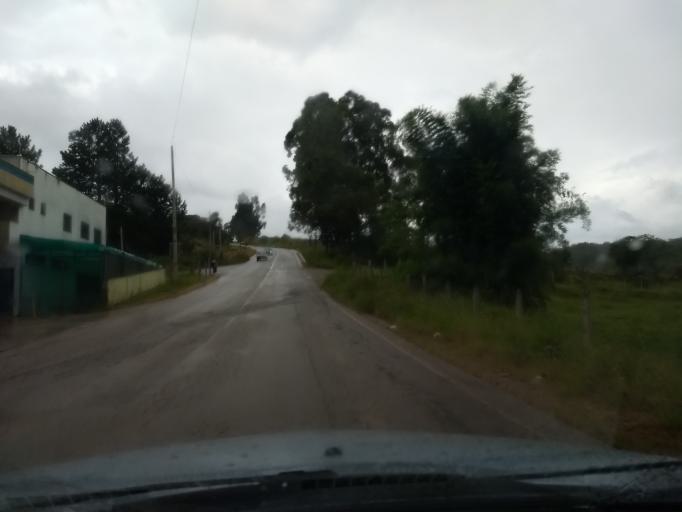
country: BR
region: Minas Gerais
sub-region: Extrema
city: Extrema
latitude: -22.7483
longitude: -46.3734
